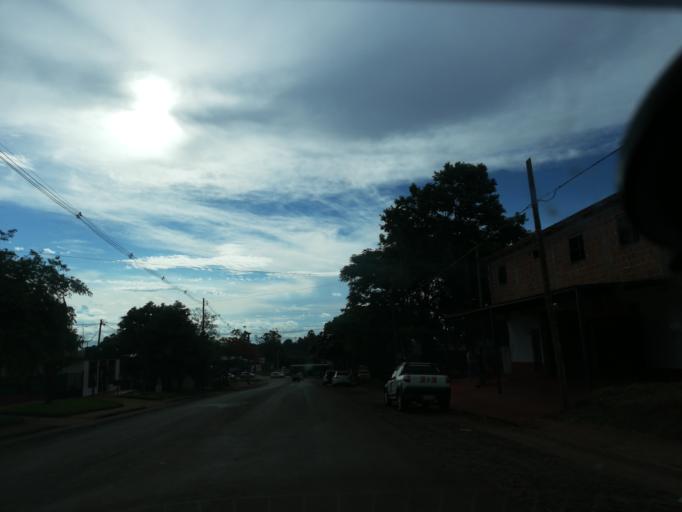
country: AR
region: Misiones
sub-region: Departamento de Capital
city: Posadas
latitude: -27.4189
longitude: -55.9291
